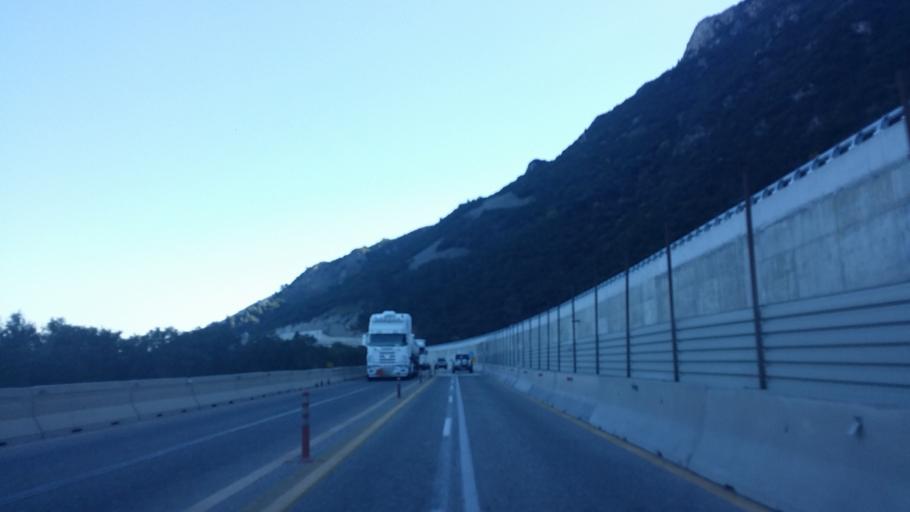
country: GR
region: West Greece
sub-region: Nomos Achaias
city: Ano Kastritsion
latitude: 38.3234
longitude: 21.9028
